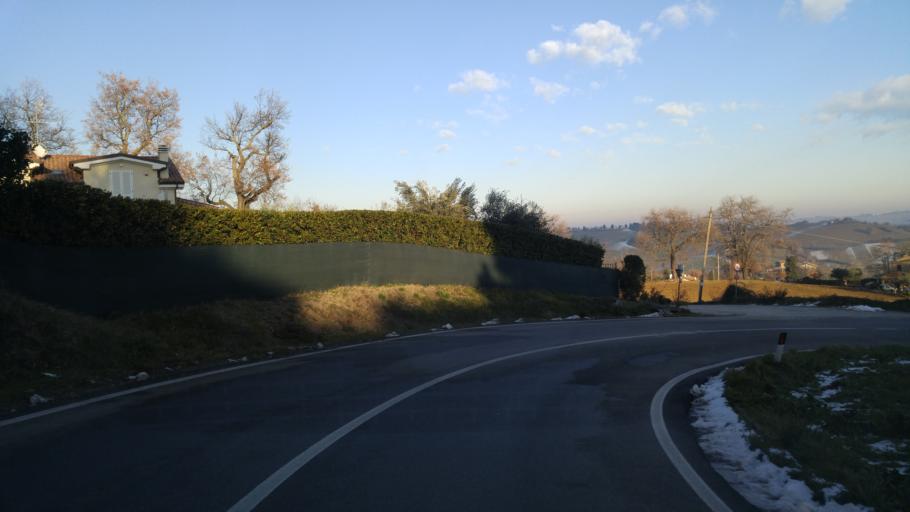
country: IT
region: The Marches
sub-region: Provincia di Pesaro e Urbino
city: Mondavio
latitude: 43.6734
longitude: 12.9715
